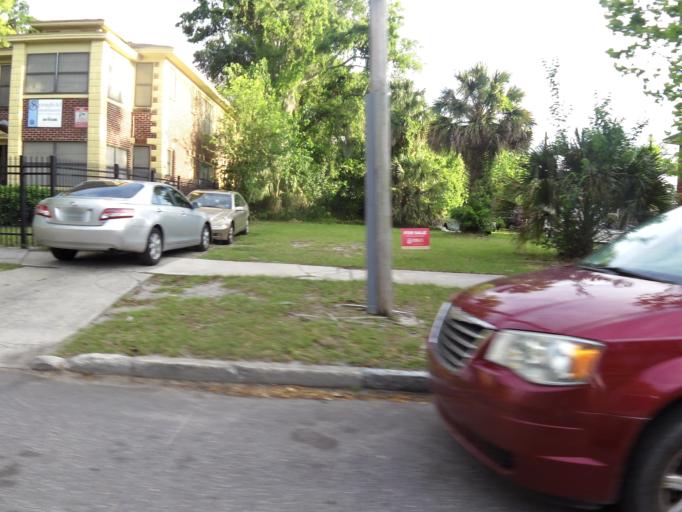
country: US
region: Florida
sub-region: Duval County
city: Jacksonville
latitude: 30.3433
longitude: -81.6567
